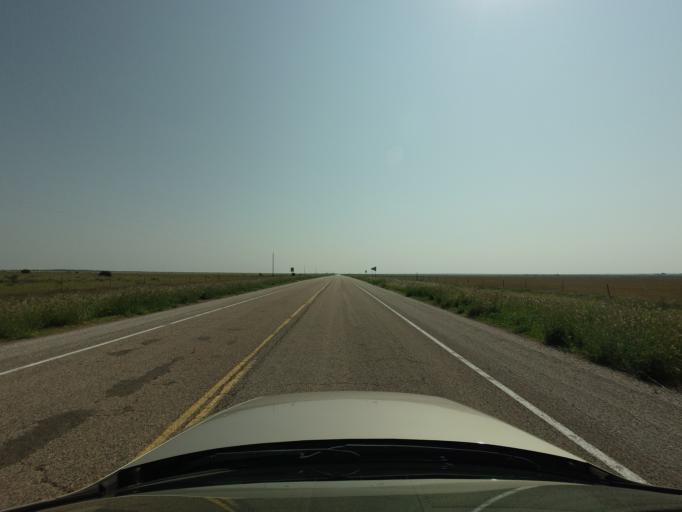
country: US
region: New Mexico
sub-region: Quay County
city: Tucumcari
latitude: 34.8234
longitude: -103.7366
